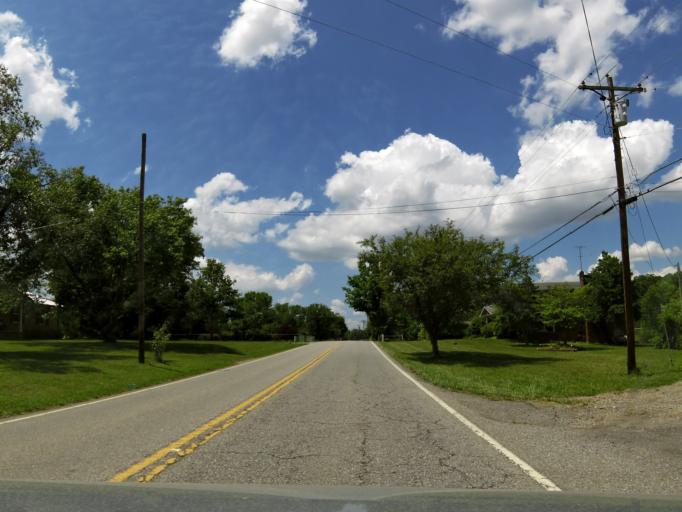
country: US
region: Tennessee
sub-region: Blount County
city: Maryville
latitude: 35.6733
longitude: -84.0449
